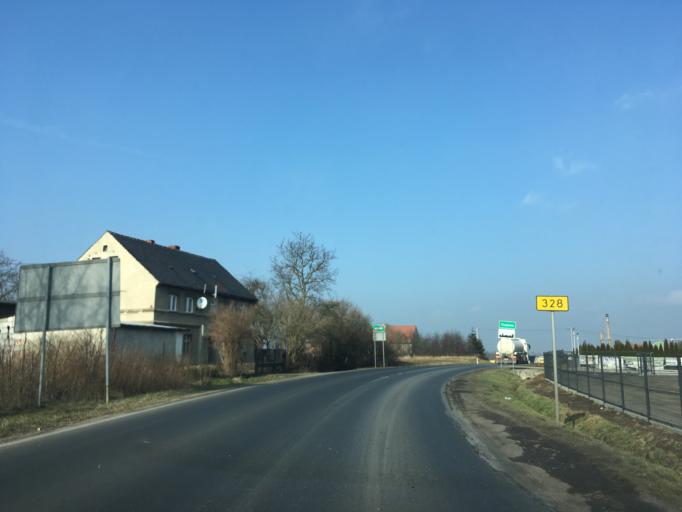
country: PL
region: Lower Silesian Voivodeship
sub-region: Powiat legnicki
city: Chojnow
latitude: 51.2632
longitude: 15.9487
